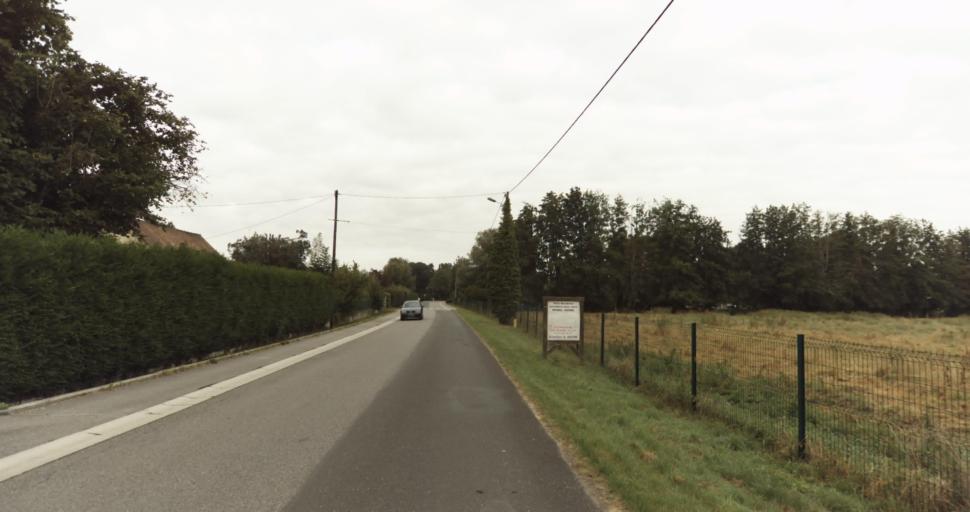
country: FR
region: Haute-Normandie
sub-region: Departement de l'Eure
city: Marcilly-sur-Eure
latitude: 48.8224
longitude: 1.3522
